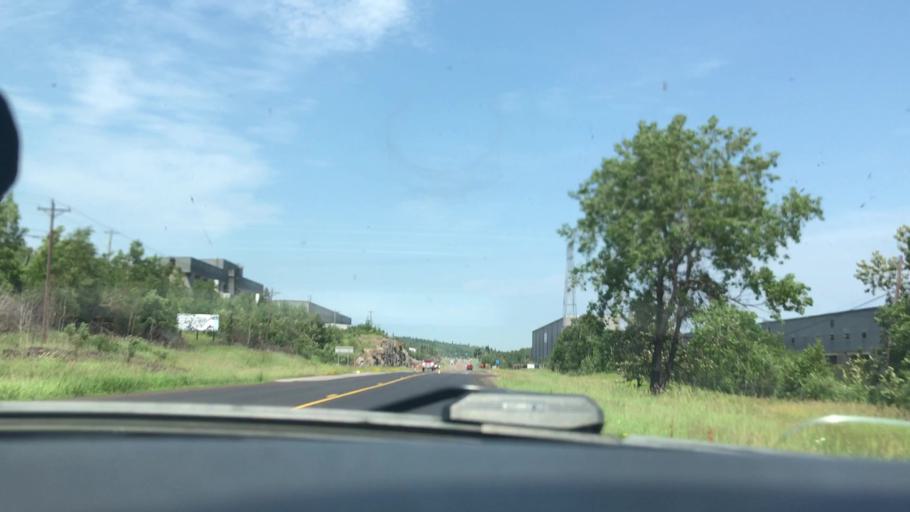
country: US
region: Minnesota
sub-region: Lake County
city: Silver Bay
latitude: 47.2865
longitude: -91.2659
